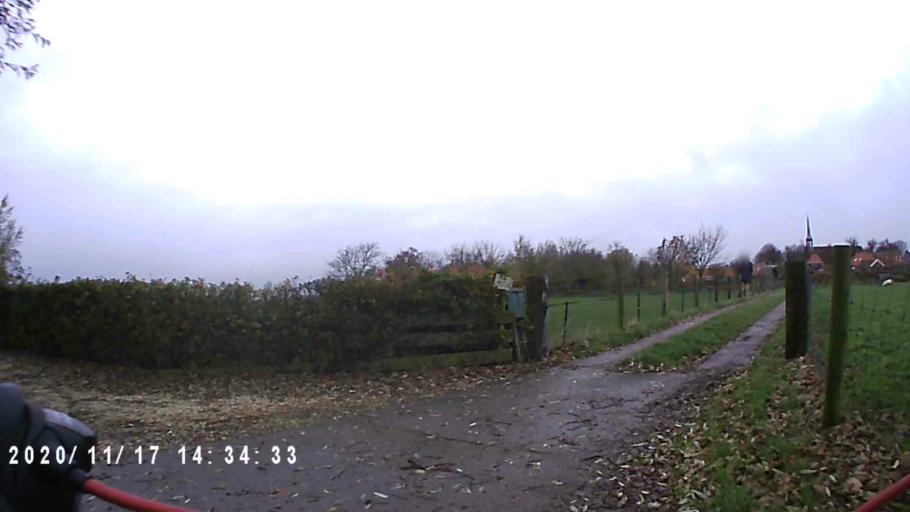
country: NL
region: Groningen
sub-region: Gemeente Zuidhorn
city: Oldehove
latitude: 53.2885
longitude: 6.3651
